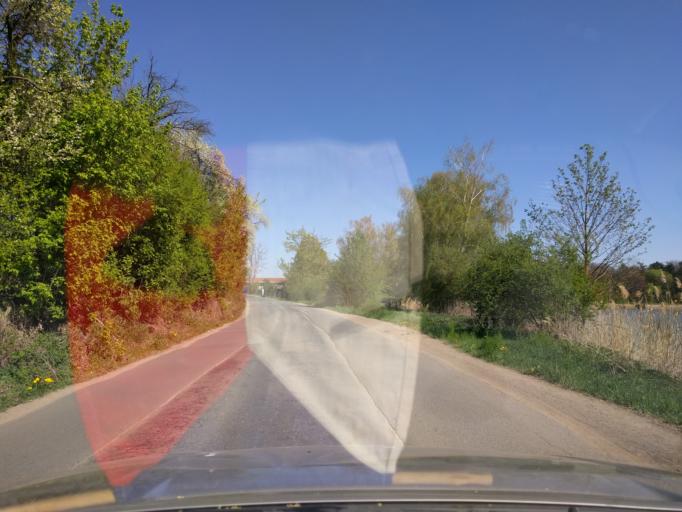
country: CZ
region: Central Bohemia
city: Cesky Brod
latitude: 50.0586
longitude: 14.8472
